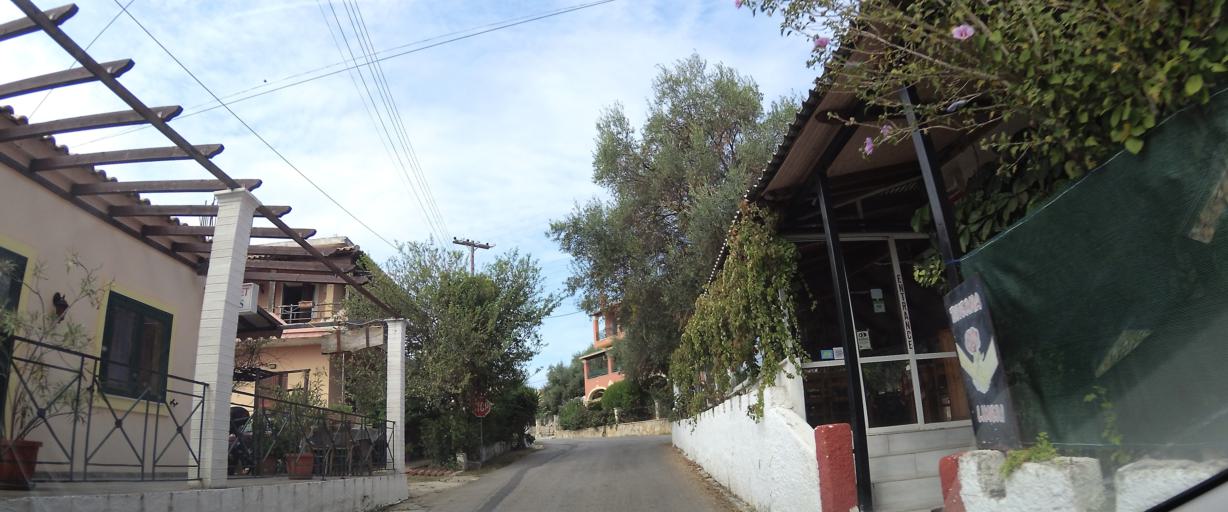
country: GR
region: Ionian Islands
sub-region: Nomos Kerkyras
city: Kontokali
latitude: 39.6888
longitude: 19.8301
